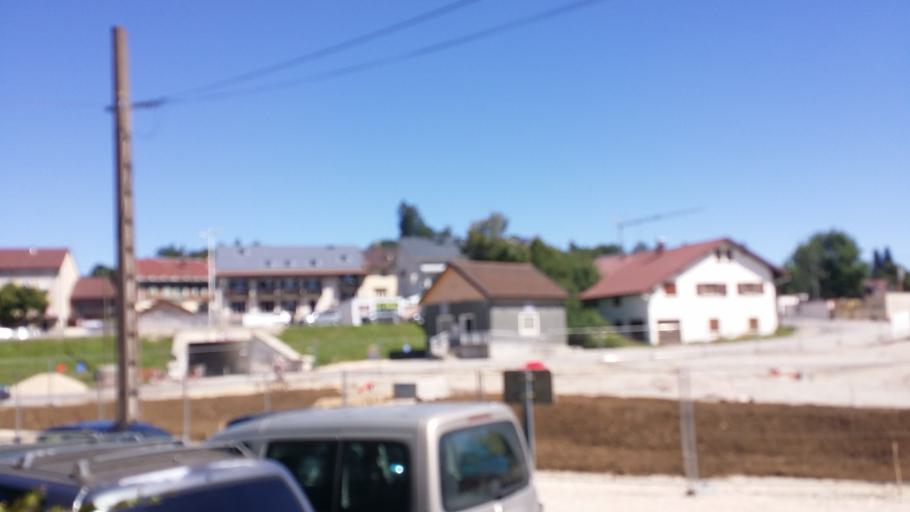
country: FR
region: Franche-Comte
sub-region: Departement du Jura
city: Les Rousses
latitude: 46.4846
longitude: 6.0585
